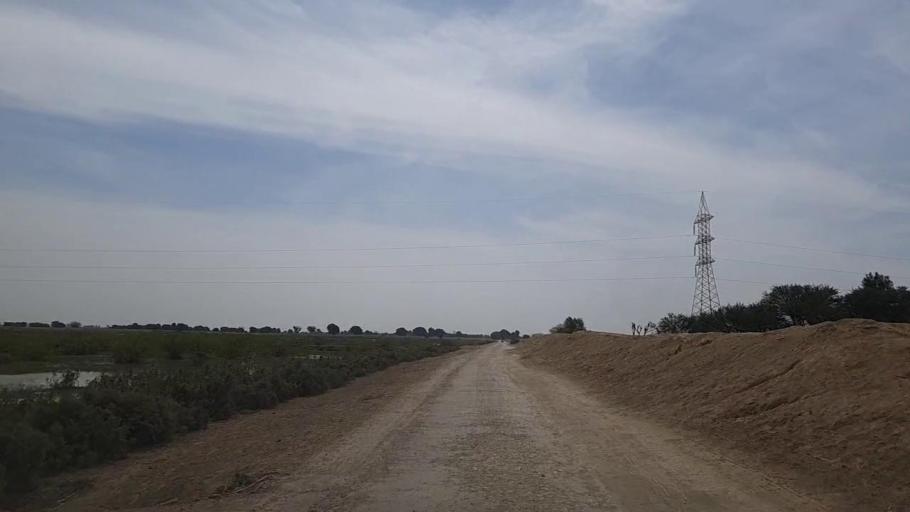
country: PK
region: Sindh
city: Samaro
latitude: 25.2939
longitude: 69.4539
